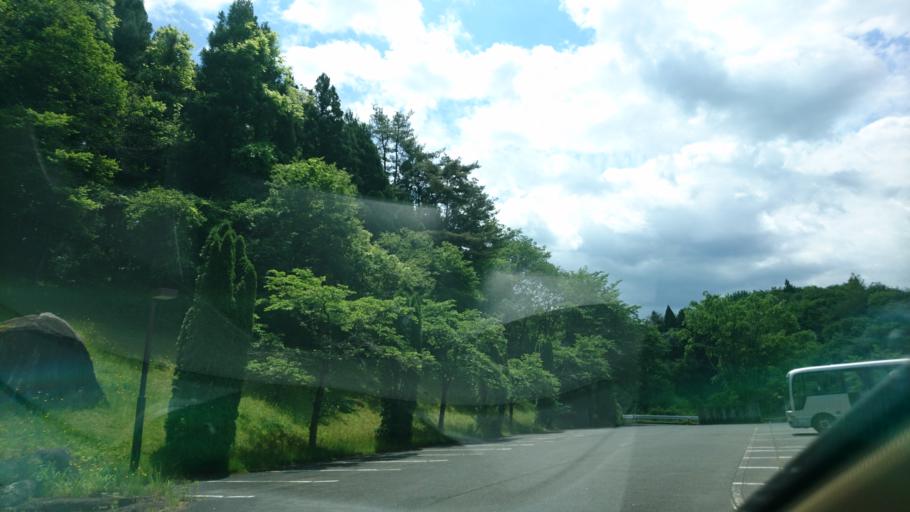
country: JP
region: Iwate
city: Ichinoseki
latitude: 38.9008
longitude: 141.3283
